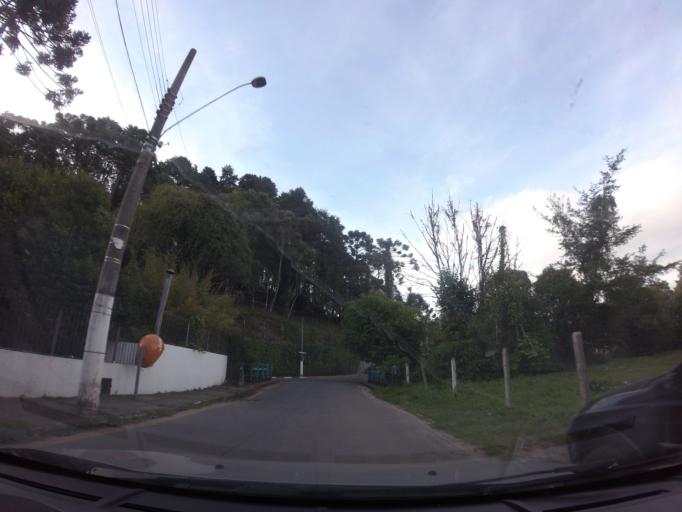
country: BR
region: Sao Paulo
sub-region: Campos Do Jordao
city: Campos do Jordao
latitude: -22.7240
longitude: -45.5680
